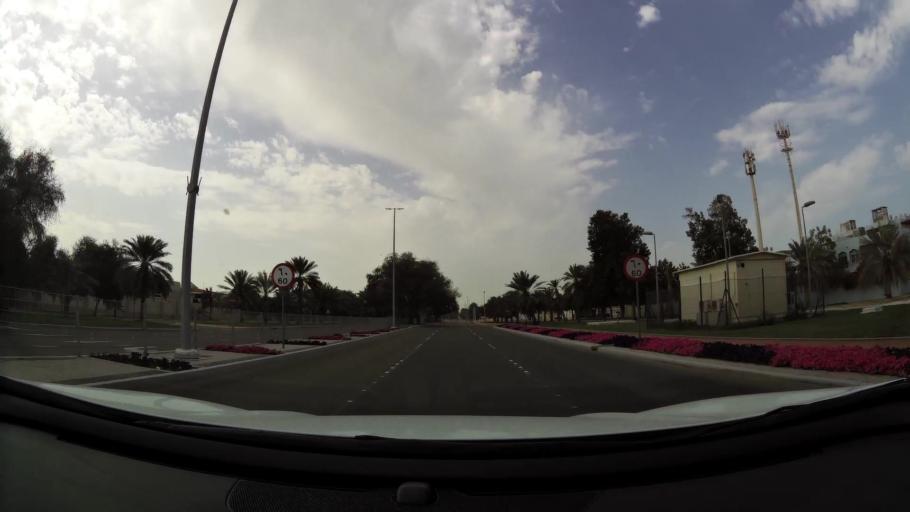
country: AE
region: Abu Dhabi
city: Abu Dhabi
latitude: 24.4499
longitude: 54.3609
